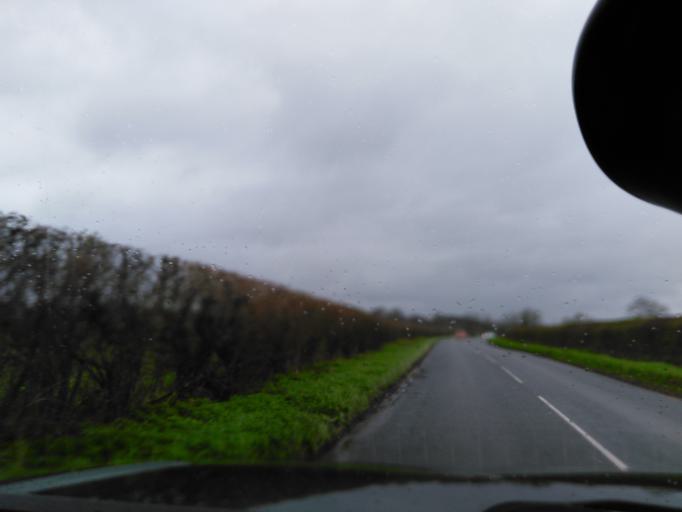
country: GB
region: England
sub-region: Wiltshire
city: Wingfield
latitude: 51.3205
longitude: -2.2578
